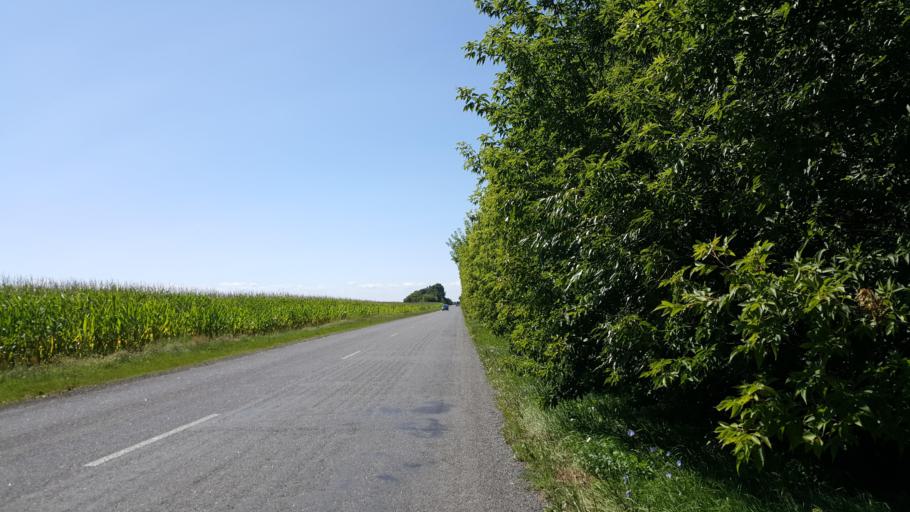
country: BY
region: Brest
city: Charnawchytsy
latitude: 52.2063
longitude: 23.8112
